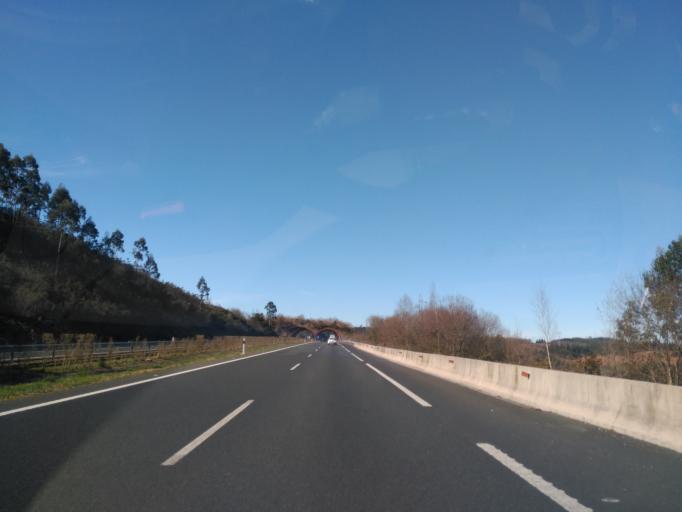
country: ES
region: Cantabria
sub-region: Provincia de Cantabria
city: Cabezon de la Sal
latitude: 43.3216
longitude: -4.2747
